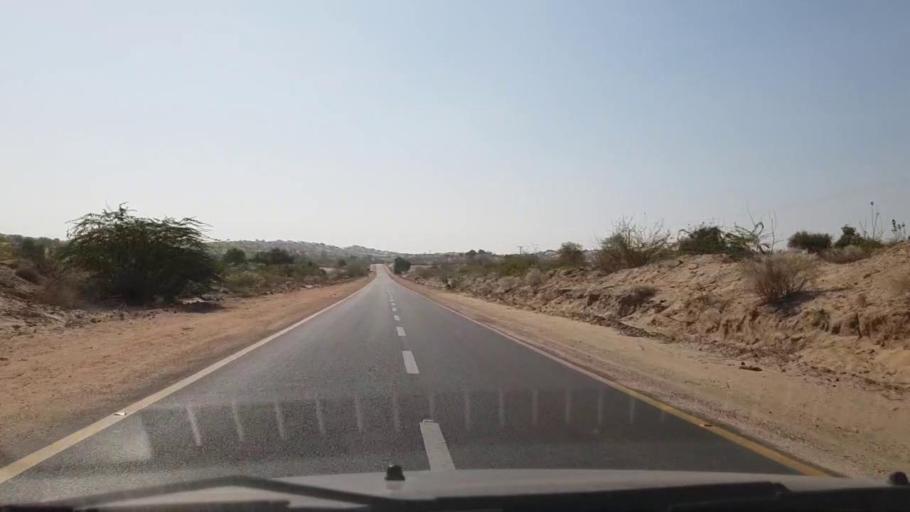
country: PK
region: Sindh
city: Diplo
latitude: 24.5016
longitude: 69.6078
